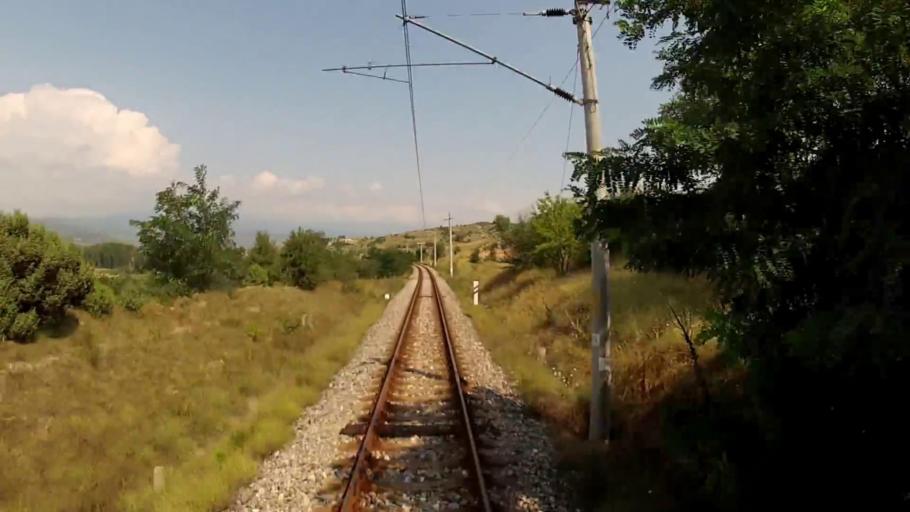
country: BG
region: Blagoevgrad
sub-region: Obshtina Strumyani
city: Strumyani
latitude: 41.6203
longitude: 23.2176
